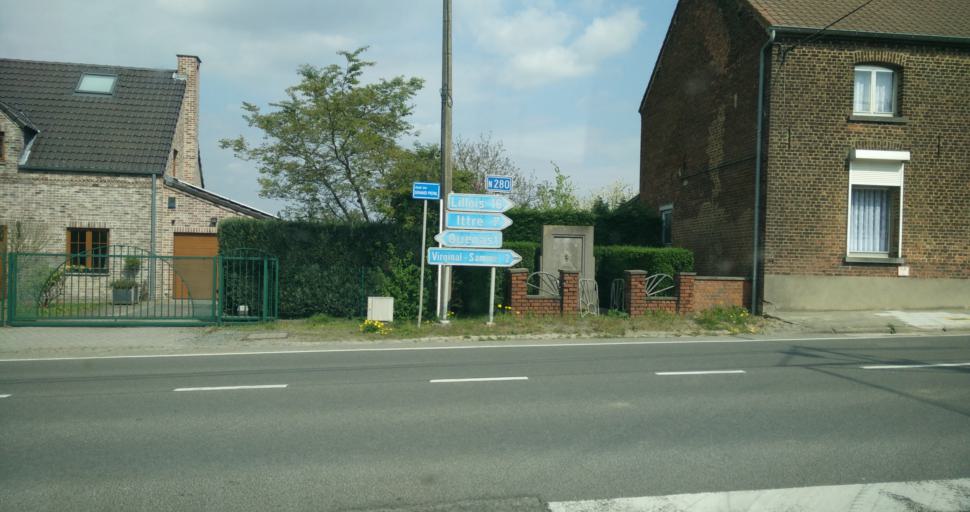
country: BE
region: Wallonia
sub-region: Province du Brabant Wallon
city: Tubize
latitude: 50.6421
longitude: 4.1917
